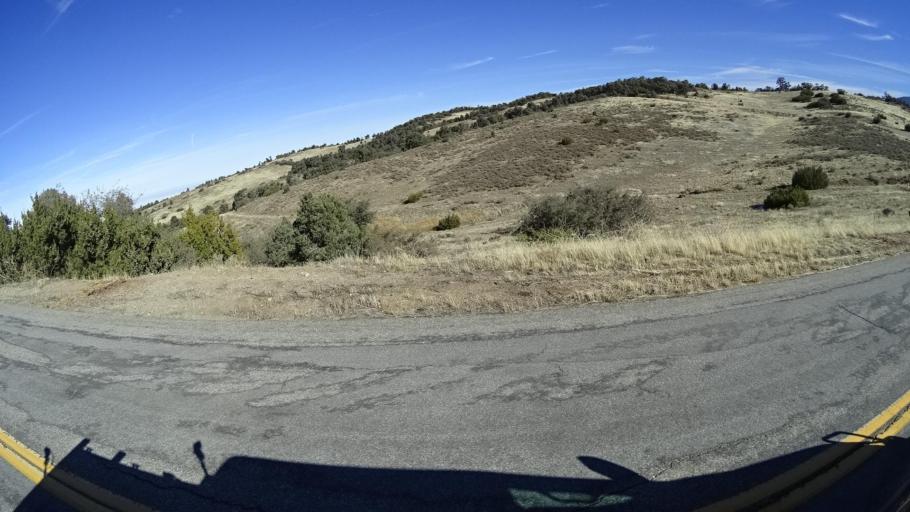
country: US
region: California
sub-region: Kern County
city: Pine Mountain Club
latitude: 34.8660
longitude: -119.3186
